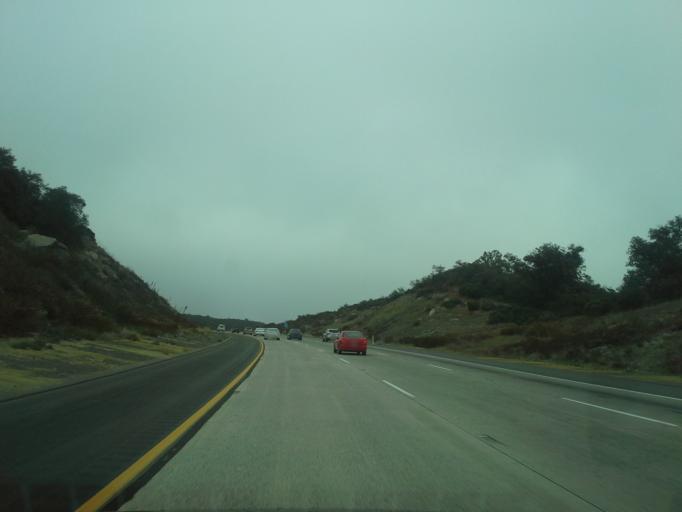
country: US
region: California
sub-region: San Diego County
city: Descanso
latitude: 32.8186
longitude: -116.5841
